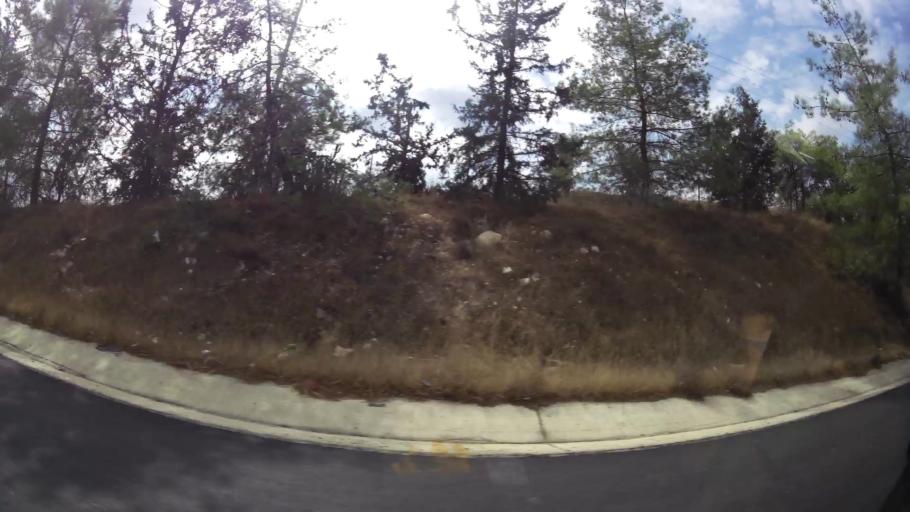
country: CY
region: Lefkosia
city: Lympia
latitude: 34.9928
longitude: 33.4520
